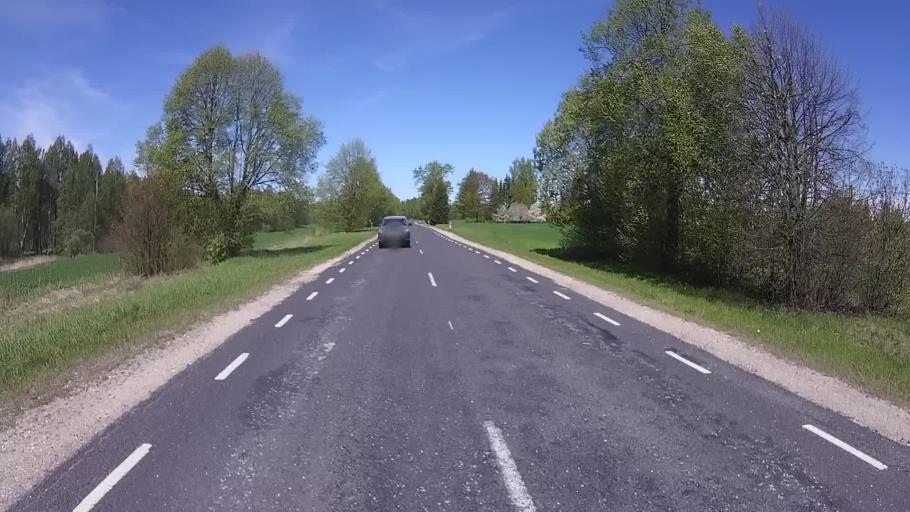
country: EE
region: Polvamaa
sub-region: Raepina vald
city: Rapina
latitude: 58.0439
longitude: 27.3901
